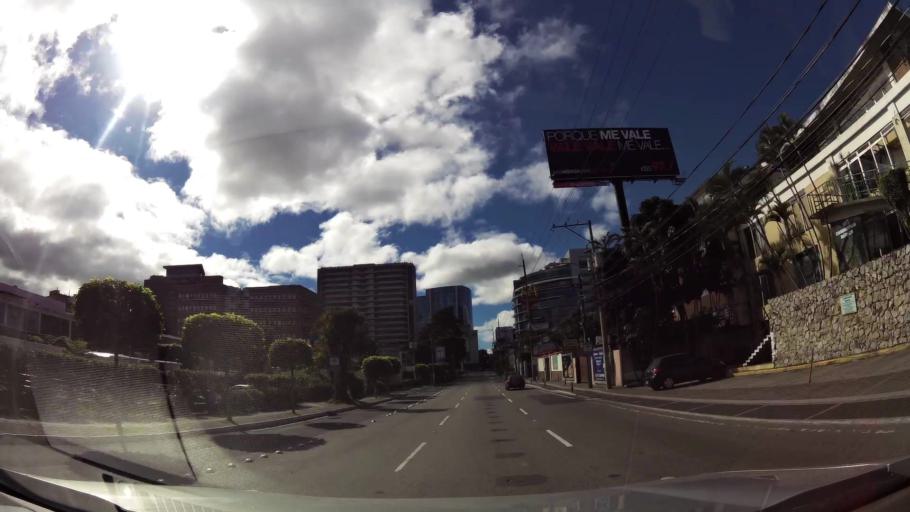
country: GT
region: Guatemala
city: Guatemala City
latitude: 14.6056
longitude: -90.5104
